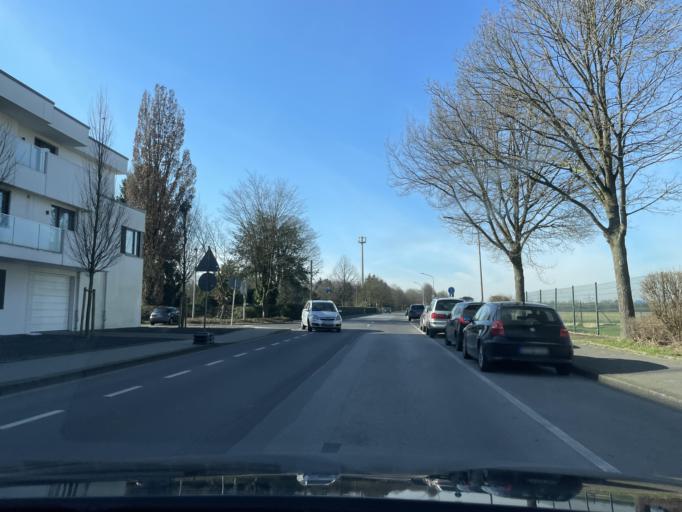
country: DE
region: North Rhine-Westphalia
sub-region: Regierungsbezirk Dusseldorf
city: Viersen
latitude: 51.2023
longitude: 6.3858
